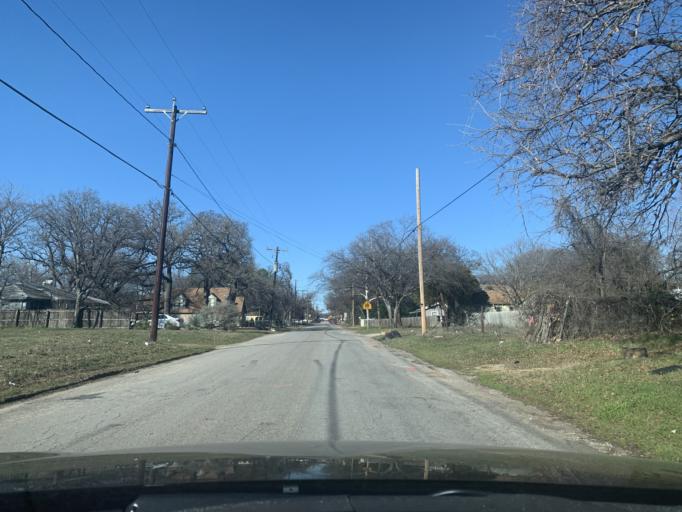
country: US
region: Texas
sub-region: Tarrant County
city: Haltom City
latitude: 32.7779
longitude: -97.2874
